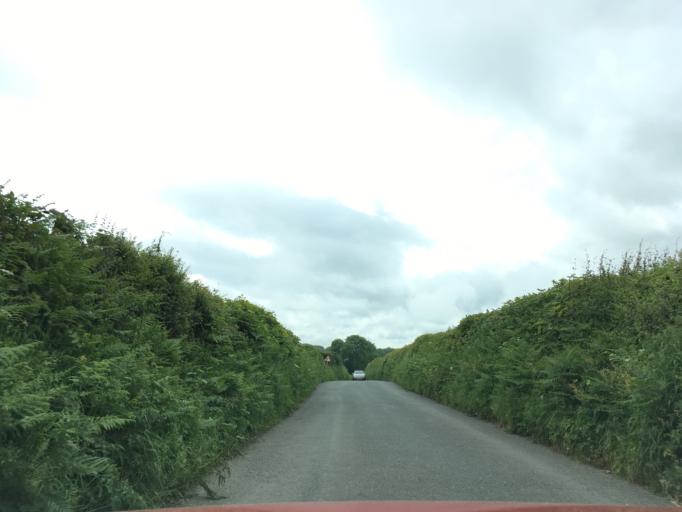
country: GB
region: England
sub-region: Devon
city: Dartmouth
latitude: 50.3343
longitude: -3.5902
